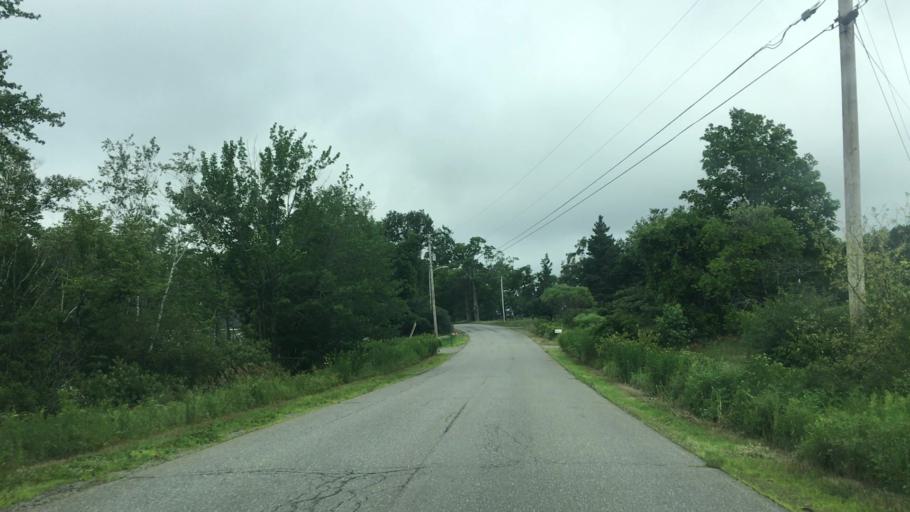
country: US
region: Maine
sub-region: Penobscot County
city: Veazie
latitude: 44.8507
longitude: -68.7454
